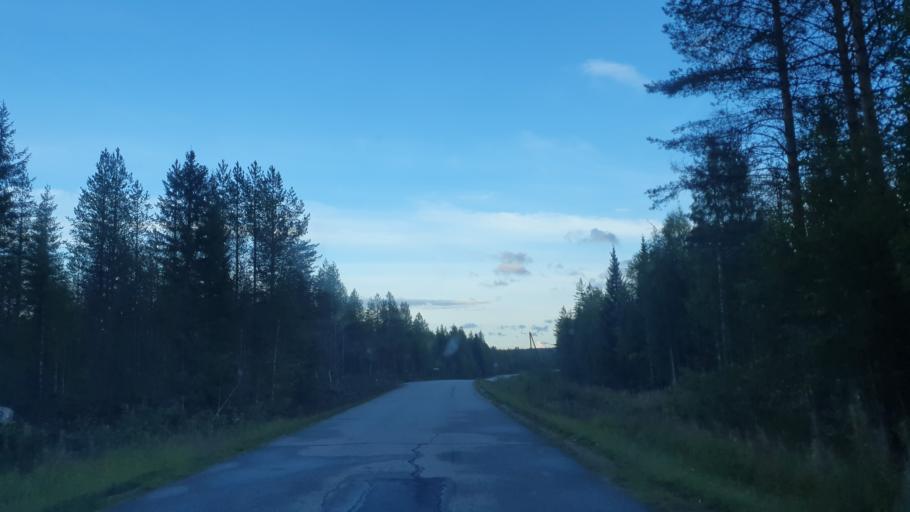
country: FI
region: Kainuu
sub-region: Kehys-Kainuu
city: Kuhmo
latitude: 64.4180
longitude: 29.9245
